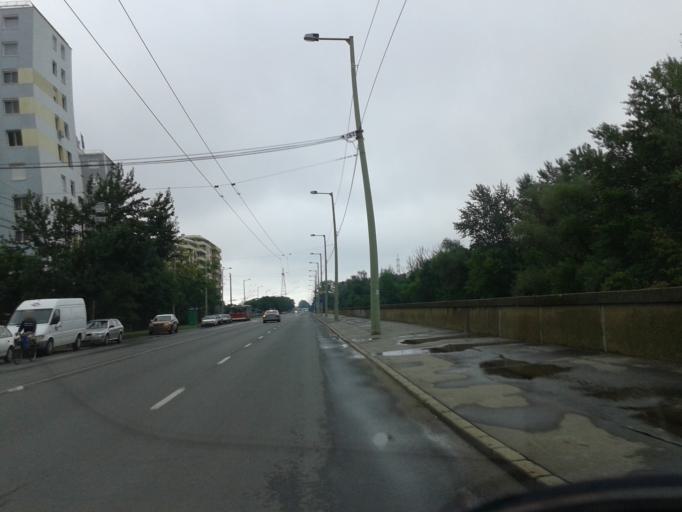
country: HU
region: Csongrad
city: Szeged
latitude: 46.2586
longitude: 20.1692
